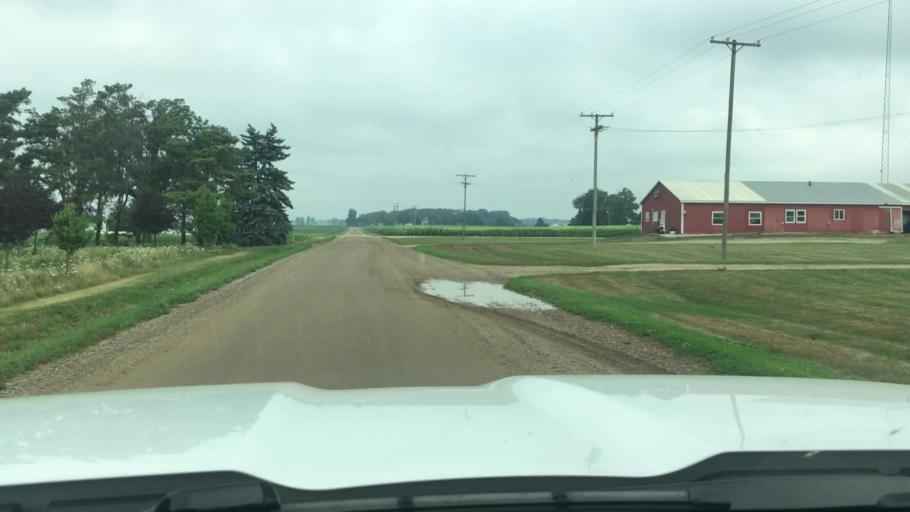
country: US
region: Michigan
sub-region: Sanilac County
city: Marlette
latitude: 43.3488
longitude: -82.9755
